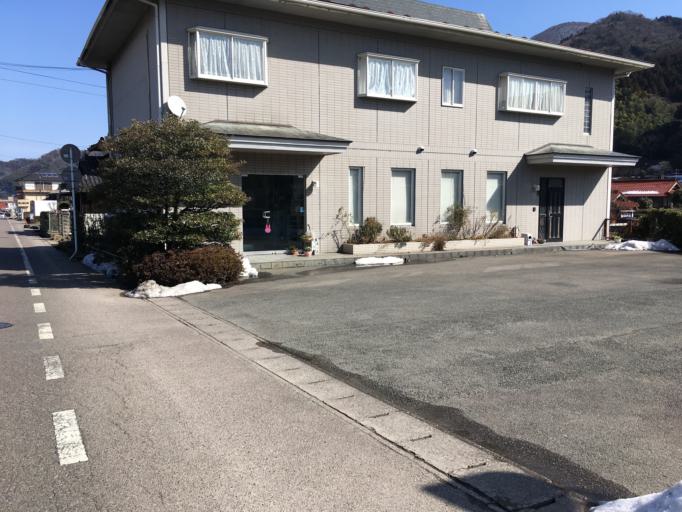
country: JP
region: Shimane
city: Masuda
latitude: 34.4557
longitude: 131.7682
